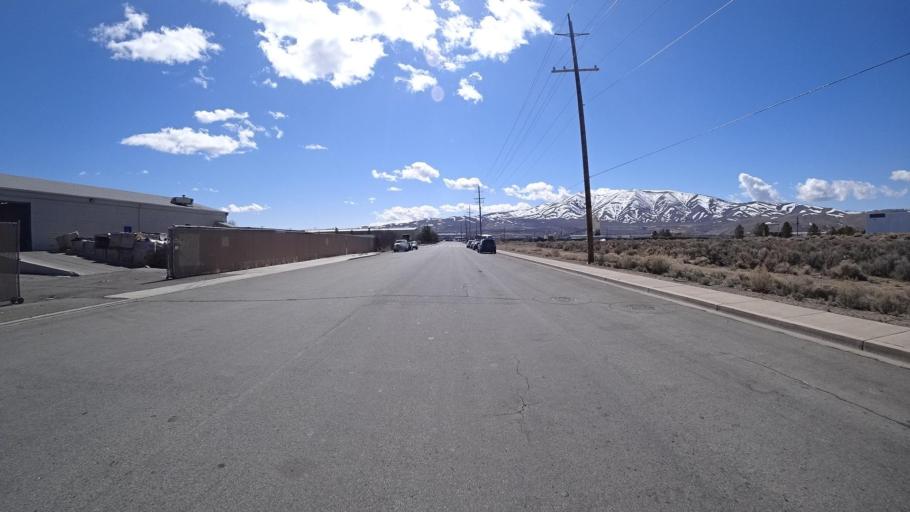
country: US
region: Nevada
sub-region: Washoe County
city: Lemmon Valley
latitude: 39.6559
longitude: -119.8864
